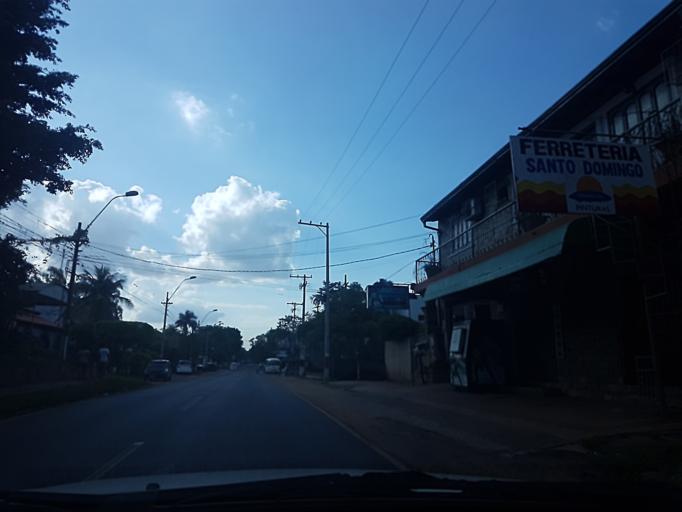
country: PY
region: Central
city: Aregua
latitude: -25.3097
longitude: -57.3814
